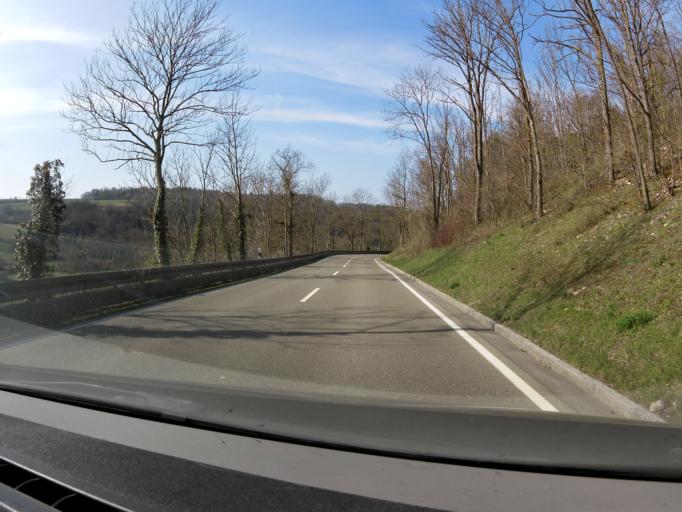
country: DE
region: Bavaria
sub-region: Regierungsbezirk Mittelfranken
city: Rothenburg ob der Tauber
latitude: 49.3842
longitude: 10.1722
